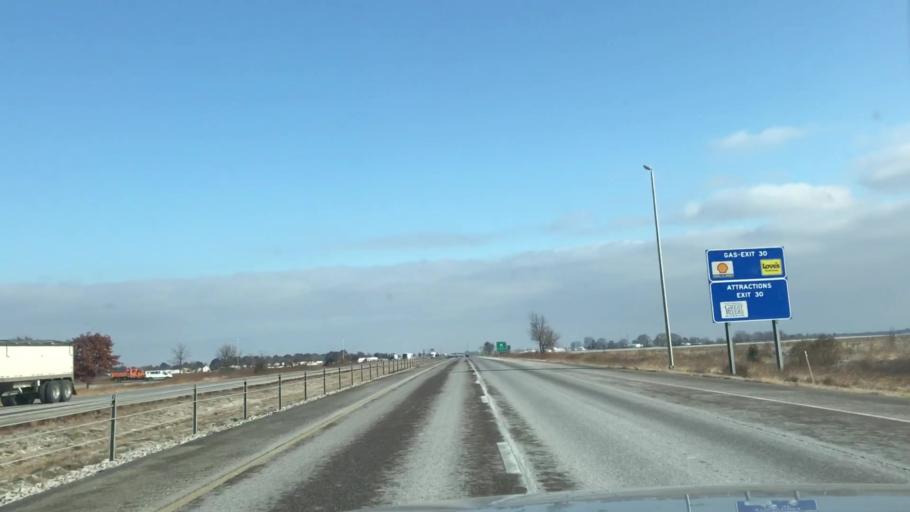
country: US
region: Illinois
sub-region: Madison County
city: Worden
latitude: 38.8708
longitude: -89.8508
